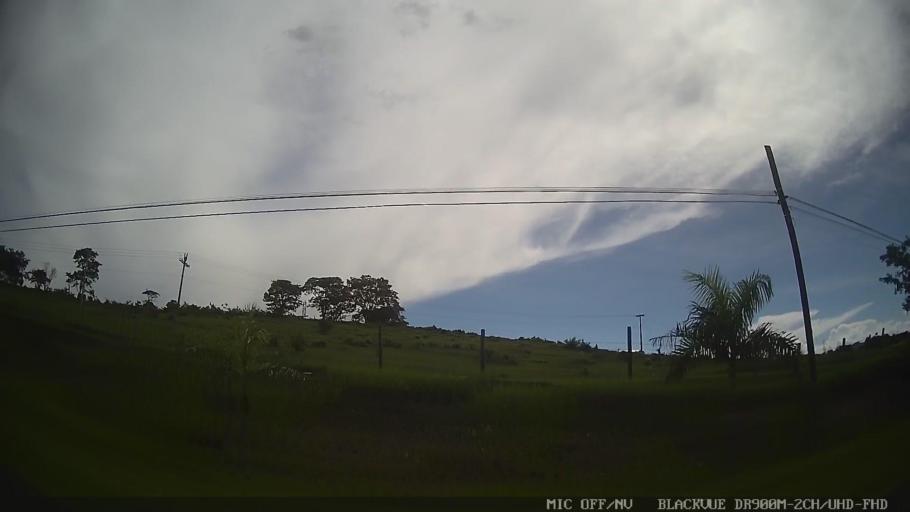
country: BR
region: Sao Paulo
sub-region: Conchas
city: Conchas
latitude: -23.0206
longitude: -47.9992
